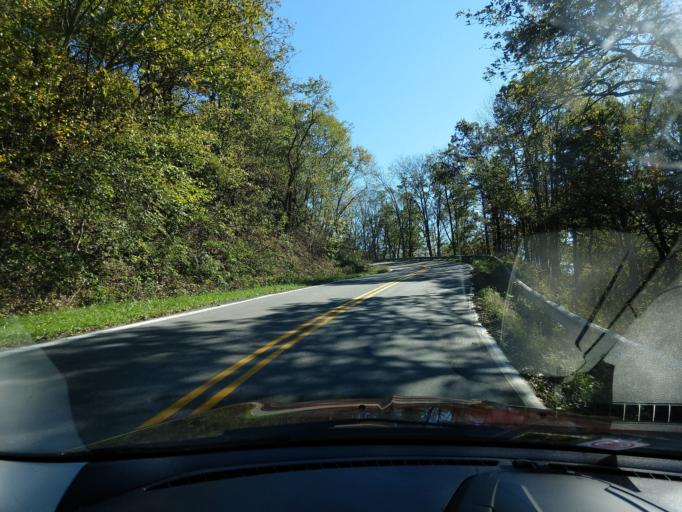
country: US
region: Virginia
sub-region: Alleghany County
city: Clifton Forge
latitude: 37.8769
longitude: -79.8881
